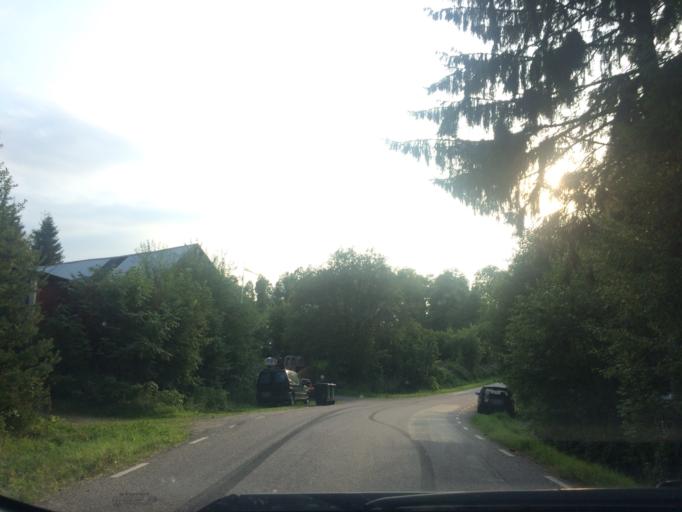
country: SE
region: Vaestra Goetaland
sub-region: Alingsas Kommun
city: Alingsas
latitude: 58.0189
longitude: 12.5334
